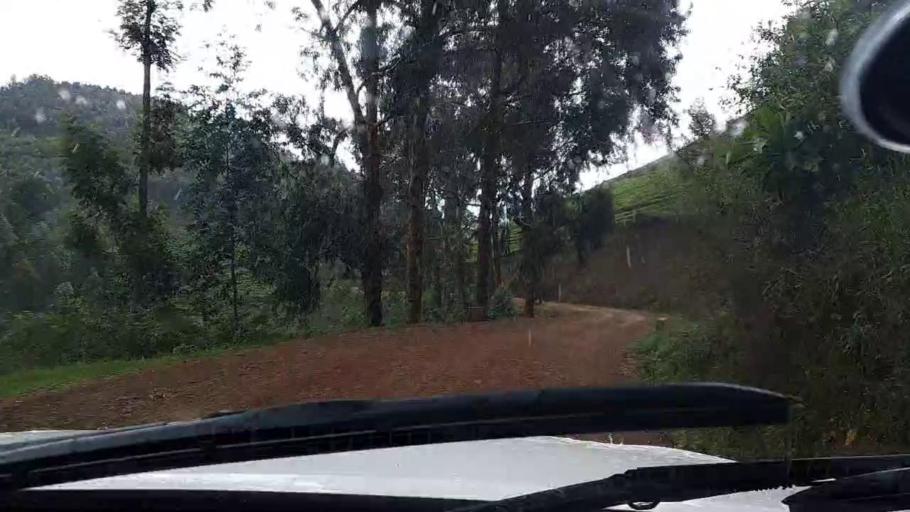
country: RW
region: Western Province
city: Kibuye
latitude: -2.1568
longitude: 29.4316
